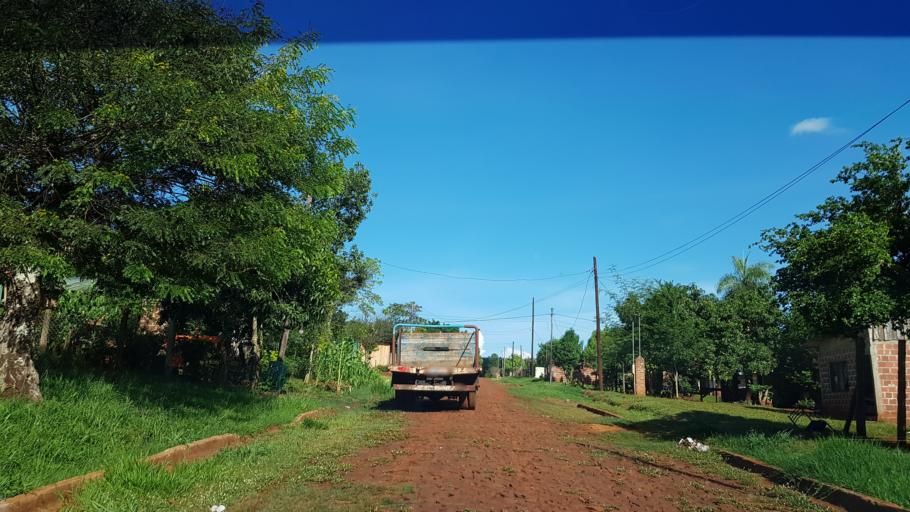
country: AR
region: Misiones
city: Puerto Libertad
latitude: -25.9128
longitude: -54.5843
